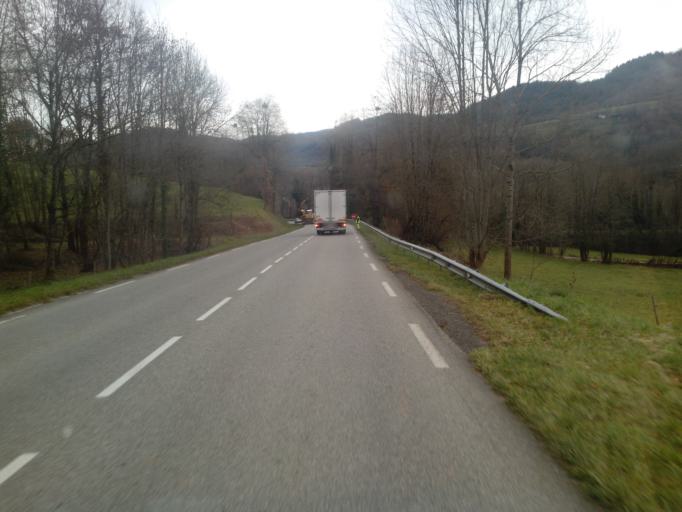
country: FR
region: Midi-Pyrenees
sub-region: Departement de l'Ariege
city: Montjoie-en-Couserans
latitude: 42.9959
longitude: 1.3140
